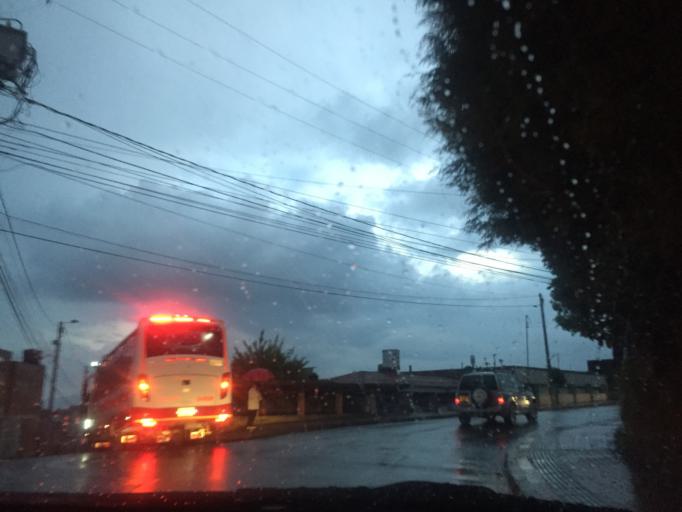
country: CO
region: Cundinamarca
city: Cogua
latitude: 5.0654
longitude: -73.9777
